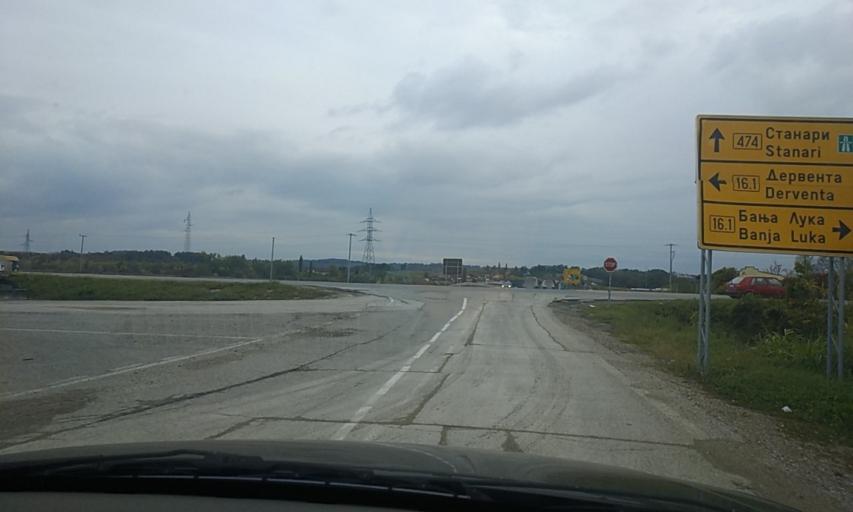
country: BA
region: Republika Srpska
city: Prnjavor
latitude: 44.8562
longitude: 17.6882
